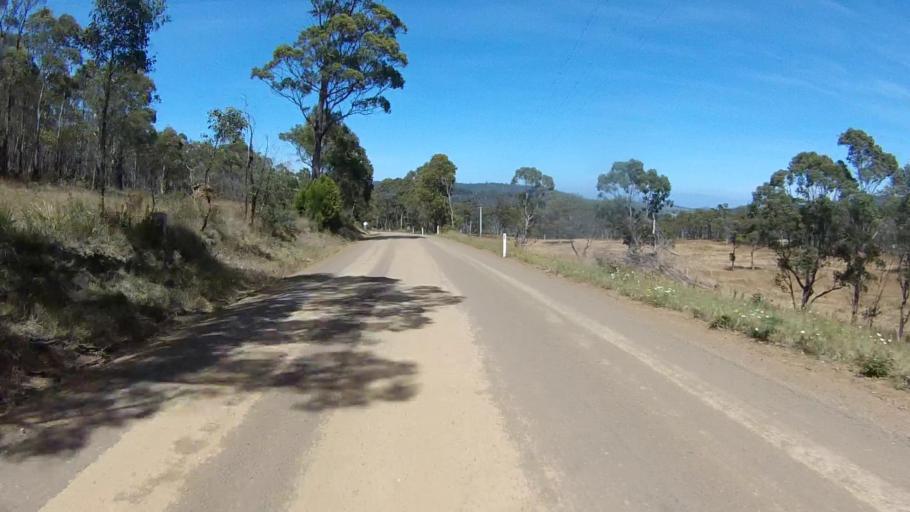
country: AU
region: Tasmania
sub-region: Sorell
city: Sorell
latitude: -42.7452
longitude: 147.7287
